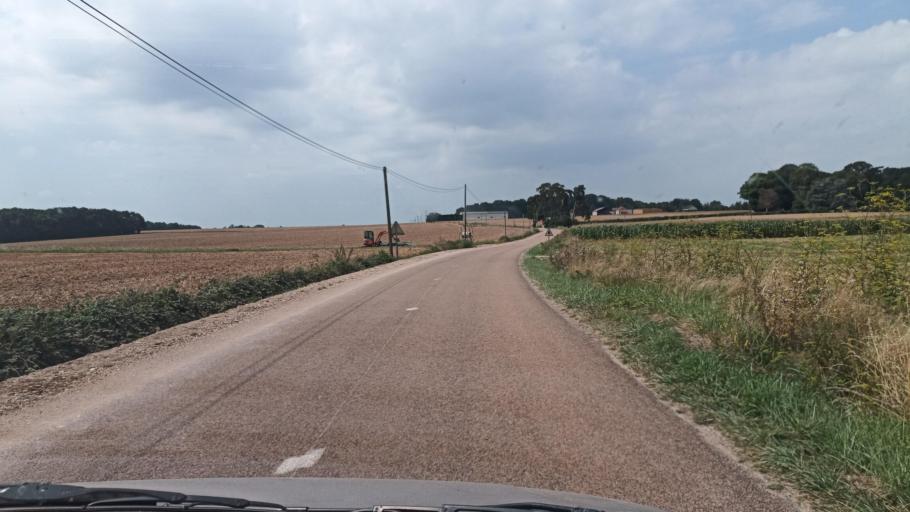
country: FR
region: Bourgogne
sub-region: Departement de l'Yonne
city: Saint-Julien-du-Sault
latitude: 48.0492
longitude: 3.2195
